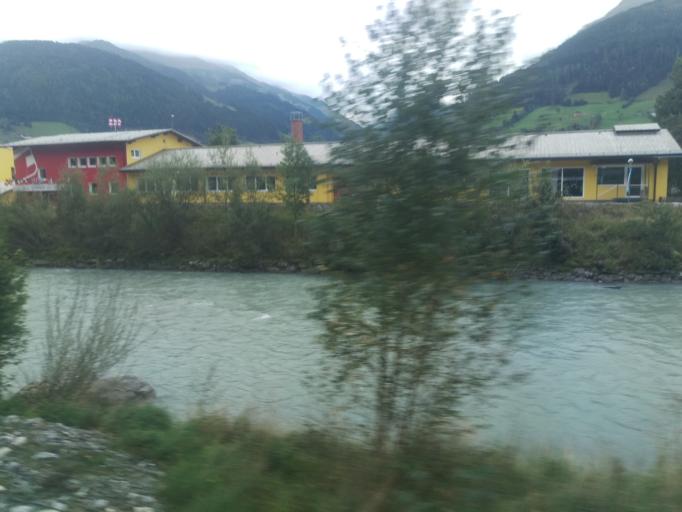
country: AT
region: Salzburg
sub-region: Politischer Bezirk Zell am See
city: Mittersill
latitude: 47.2841
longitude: 12.4747
